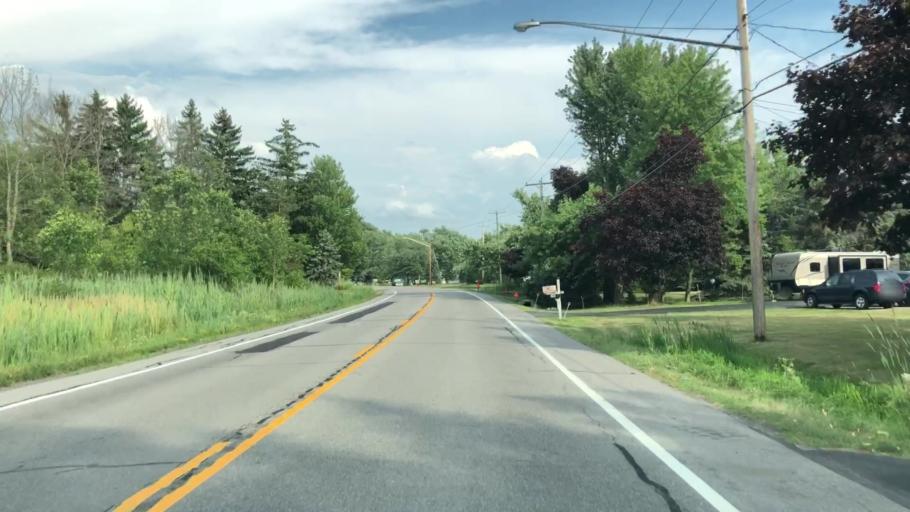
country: US
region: New York
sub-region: Erie County
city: Elma Center
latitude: 42.8563
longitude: -78.6705
